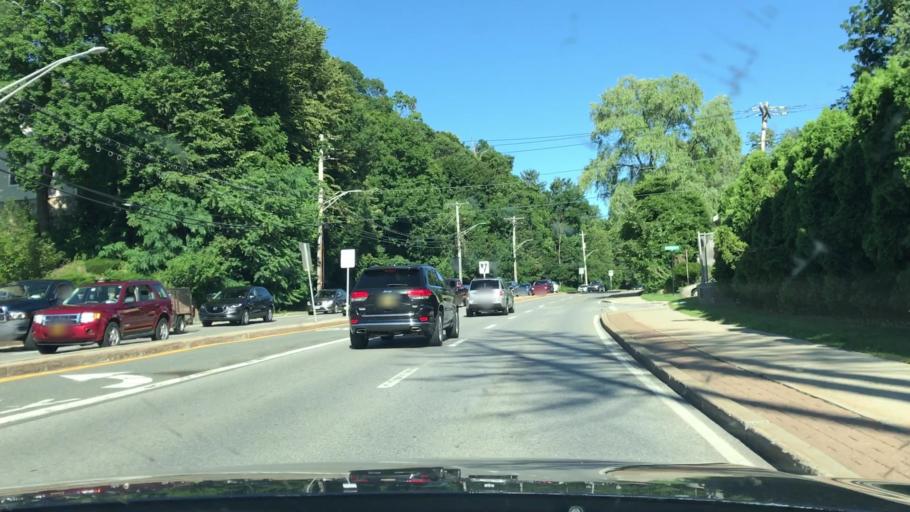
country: US
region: New York
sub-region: Westchester County
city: Thornwood
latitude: 41.1236
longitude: -73.7790
